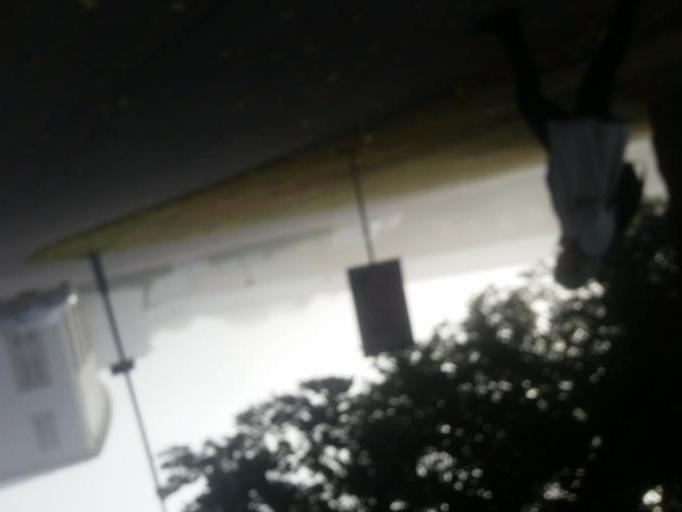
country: SE
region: Stockholm
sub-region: Stockholms Kommun
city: OEstermalm
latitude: 59.3334
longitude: 18.1152
